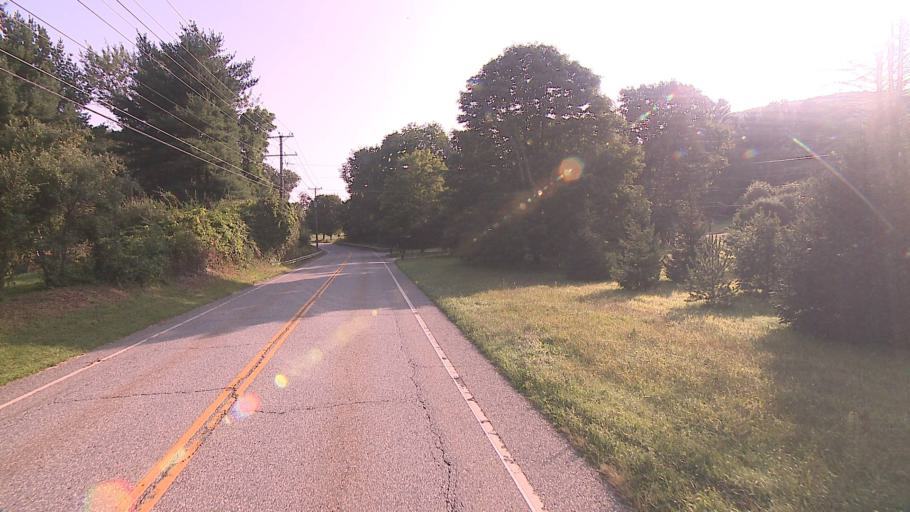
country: US
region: Connecticut
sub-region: Litchfield County
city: Kent
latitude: 41.7851
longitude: -73.4089
